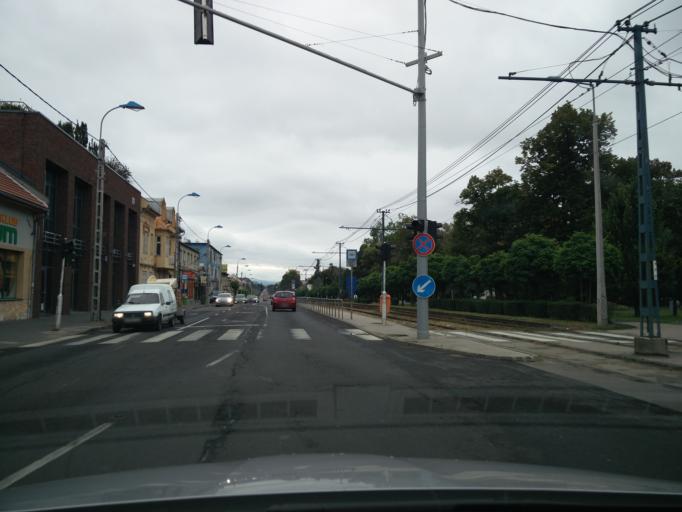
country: HU
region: Budapest
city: Budapest XVIII. keruelet
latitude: 47.4426
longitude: 19.1798
